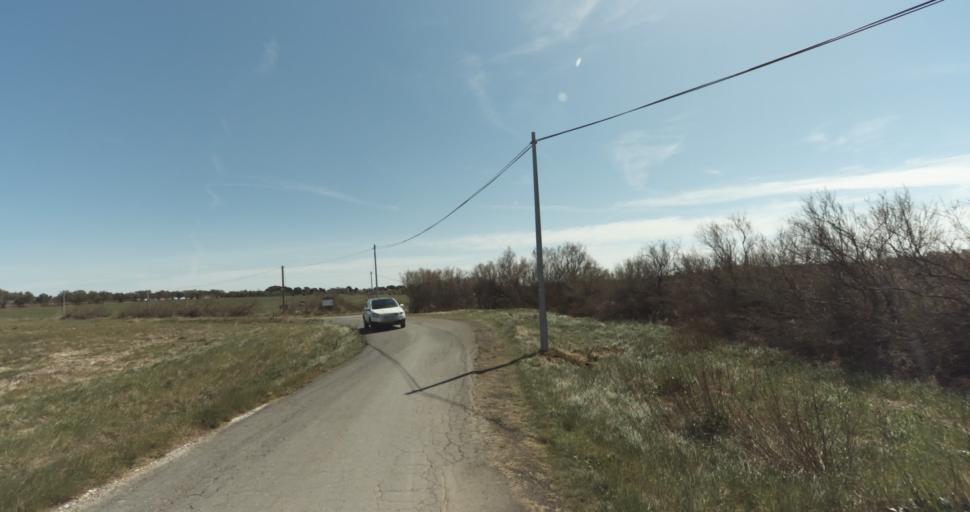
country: FR
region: Languedoc-Roussillon
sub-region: Departement de l'Herault
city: Marseillan
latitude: 43.3870
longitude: 3.5483
